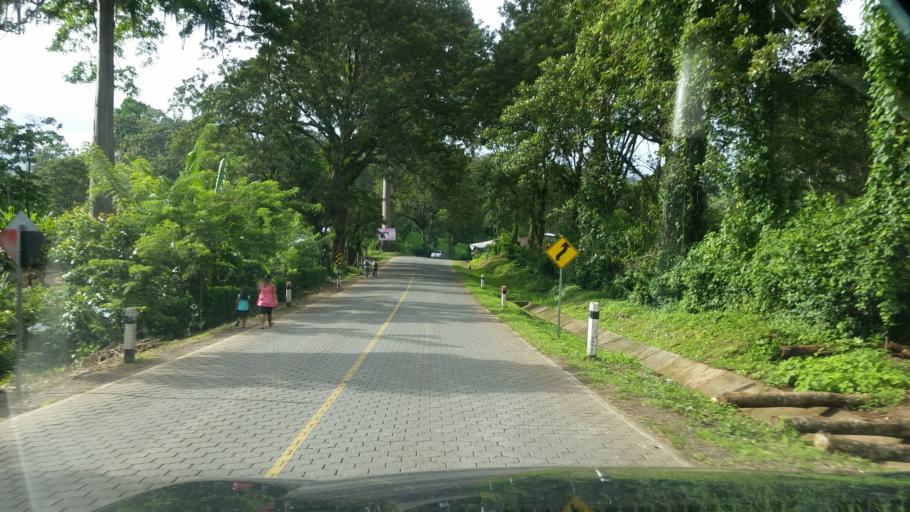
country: NI
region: Matagalpa
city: San Ramon
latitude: 13.1500
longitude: -85.7348
